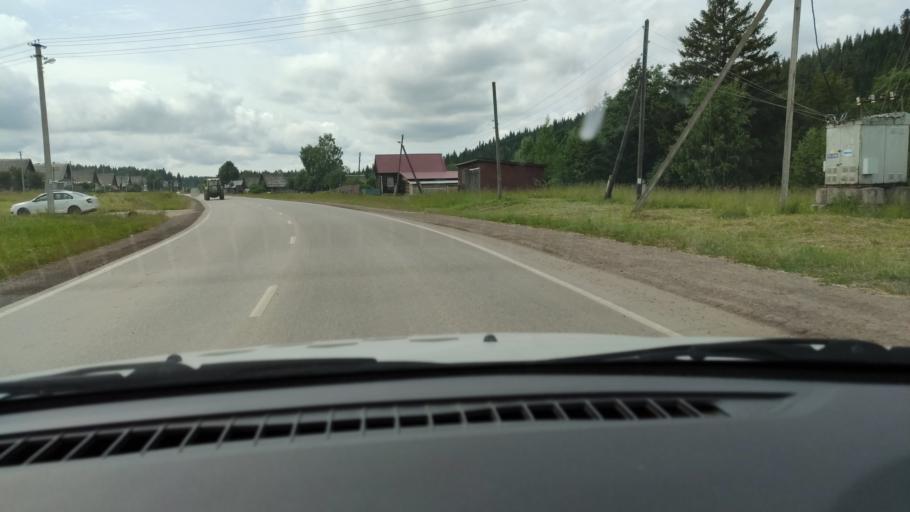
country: RU
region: Perm
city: Kukushtan
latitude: 57.4503
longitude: 56.5111
